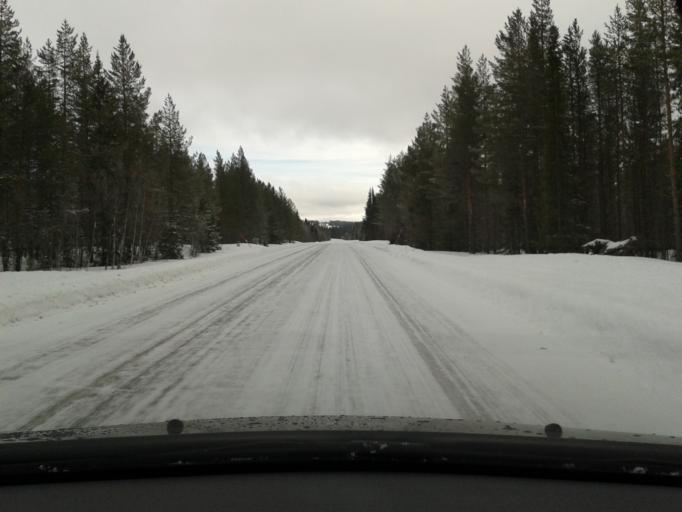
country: SE
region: Vaesterbotten
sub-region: Vilhelmina Kommun
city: Sjoberg
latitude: 64.8068
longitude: 15.9869
